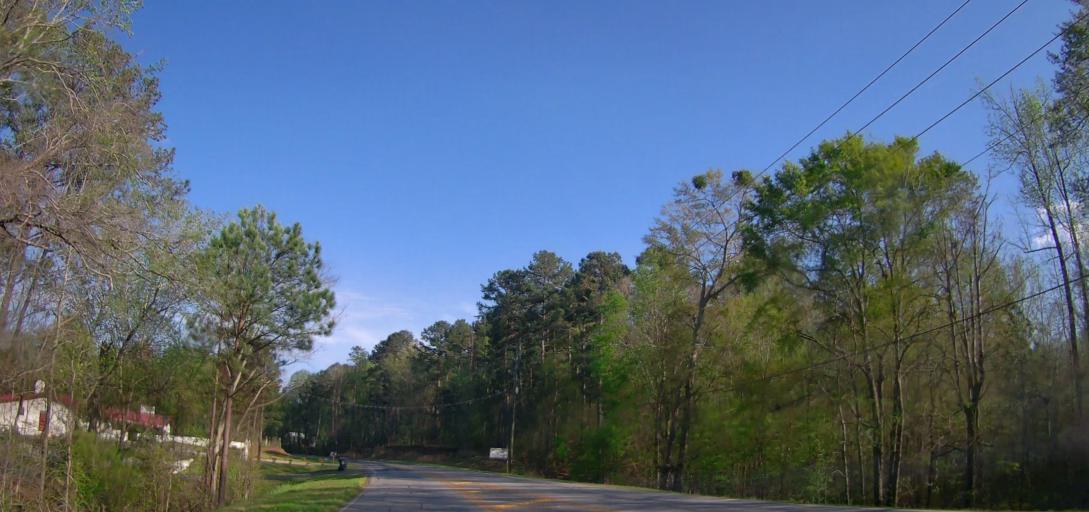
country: US
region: Georgia
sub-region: Baldwin County
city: Milledgeville
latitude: 33.1349
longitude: -83.2345
